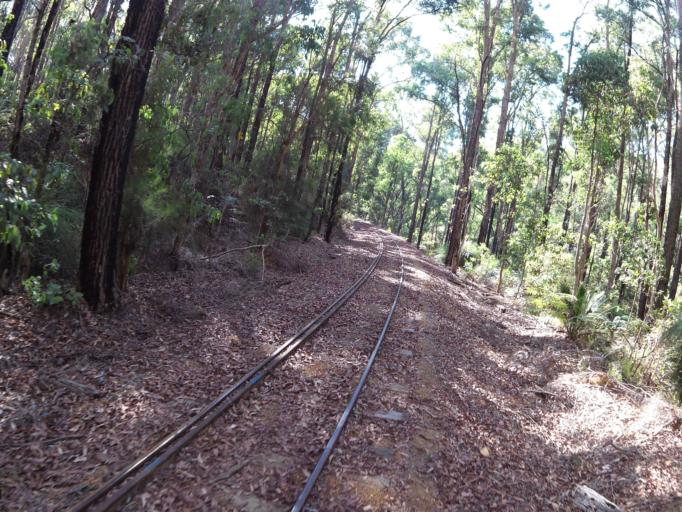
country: AU
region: Western Australia
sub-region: Waroona
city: Waroona
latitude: -32.7277
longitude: 116.1119
